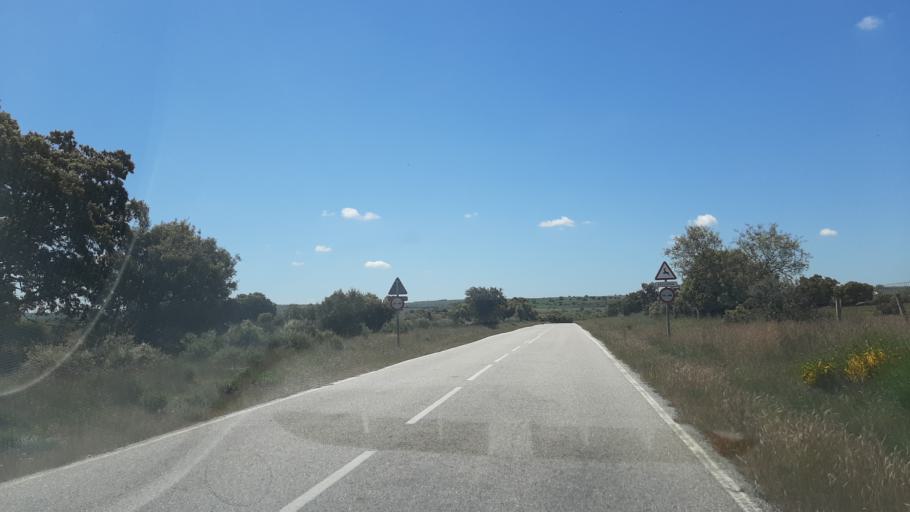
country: ES
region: Castille and Leon
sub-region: Provincia de Salamanca
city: Villarmuerto
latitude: 41.0390
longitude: -6.3929
